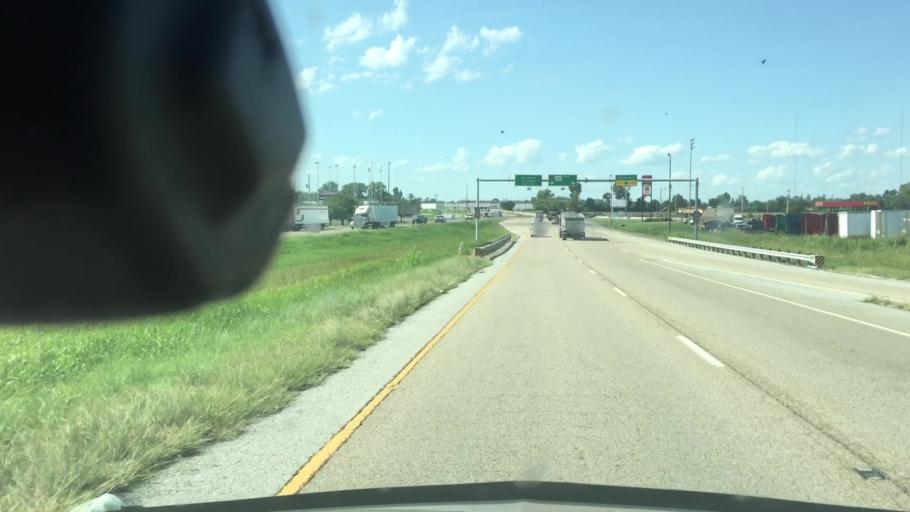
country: US
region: Illinois
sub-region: Saint Clair County
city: East Saint Louis
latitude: 38.6497
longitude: -90.1322
